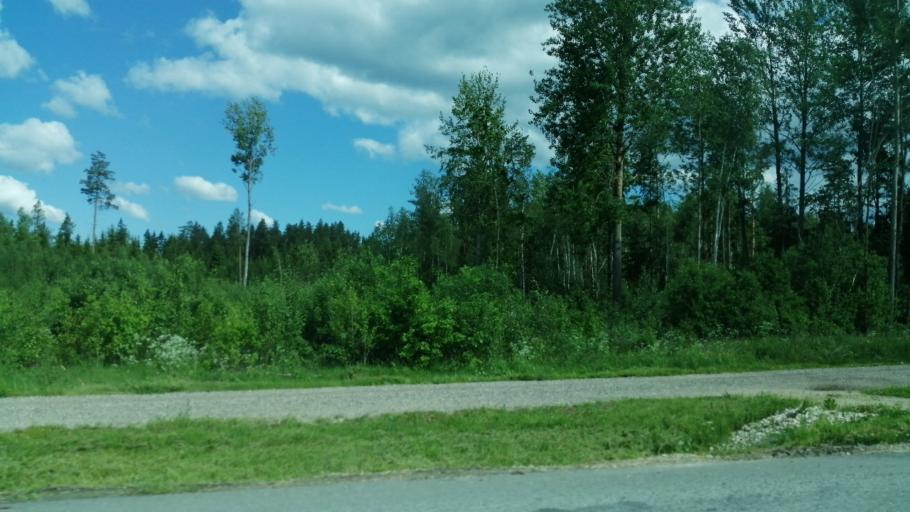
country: EE
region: Polvamaa
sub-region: Polva linn
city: Polva
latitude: 58.0521
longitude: 27.0379
